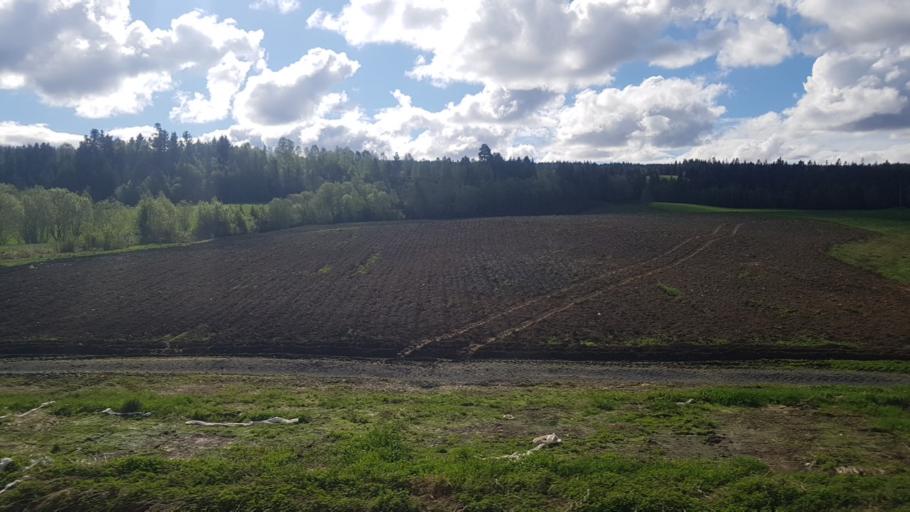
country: NO
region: Sor-Trondelag
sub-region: Rennebu
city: Berkak
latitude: 62.8922
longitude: 10.0984
